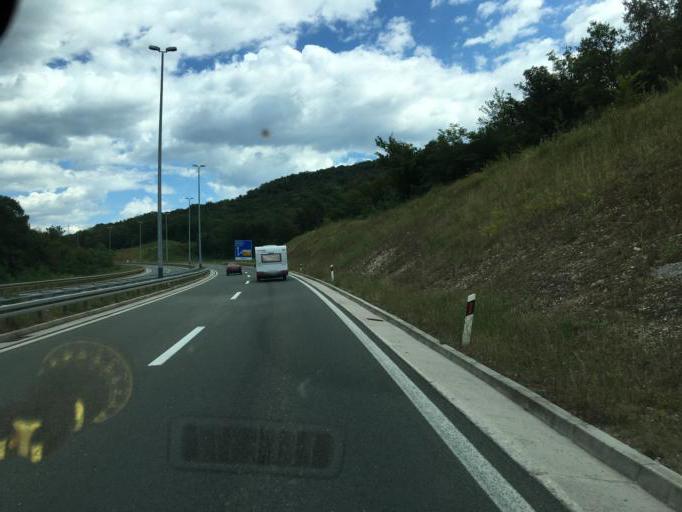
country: HR
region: Primorsko-Goranska
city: Skrljevo
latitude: 45.3150
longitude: 14.5118
